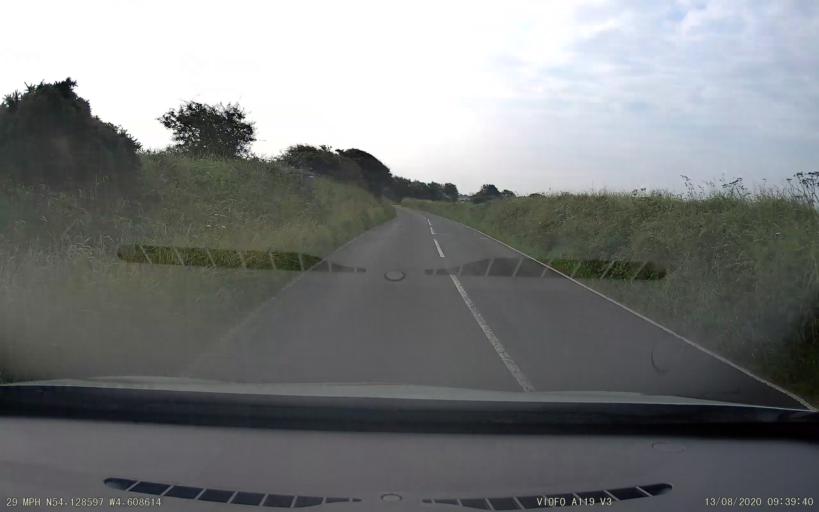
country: IM
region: Castletown
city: Castletown
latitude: 54.1285
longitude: -4.6086
